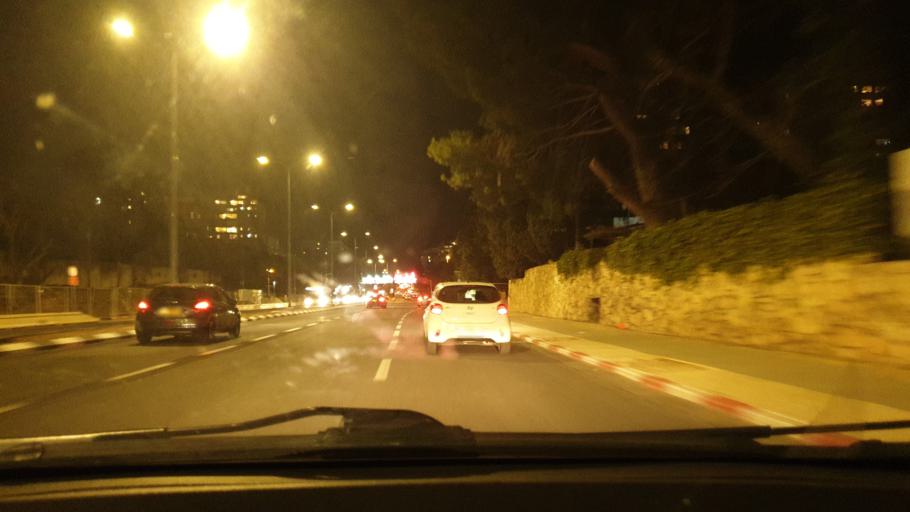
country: IL
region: Tel Aviv
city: Ramat Gan
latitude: 32.1211
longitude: 34.8043
